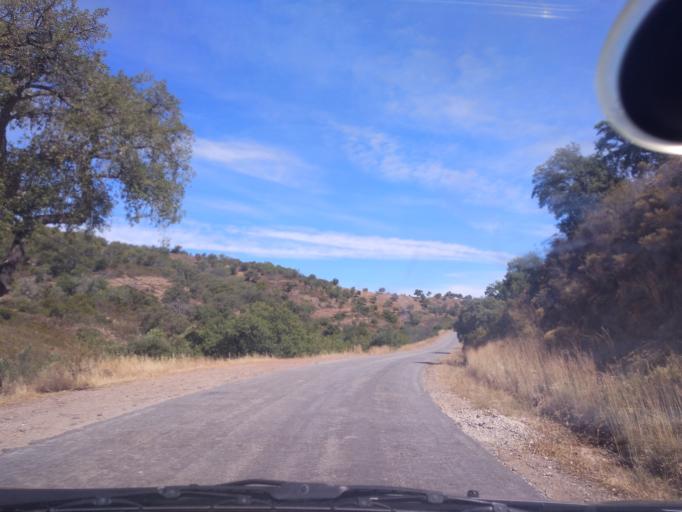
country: PT
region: Faro
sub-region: Olhao
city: Moncarapacho
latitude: 37.1558
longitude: -7.7975
